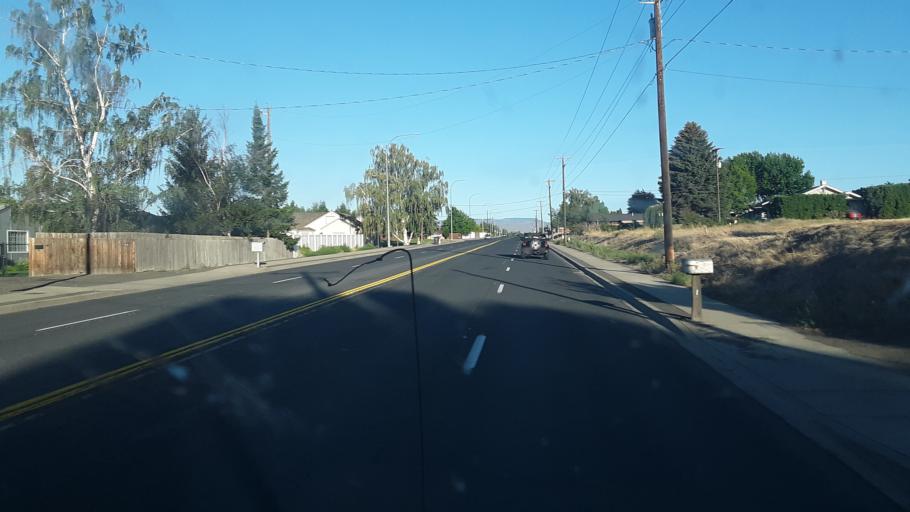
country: US
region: Washington
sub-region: Yakima County
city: West Valley
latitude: 46.6003
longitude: -120.6290
